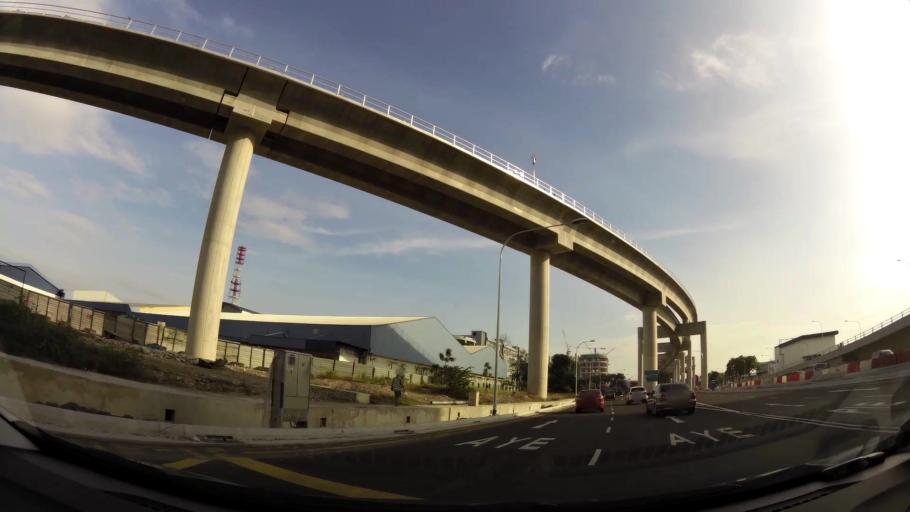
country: MY
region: Johor
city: Johor Bahru
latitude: 1.3158
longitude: 103.6566
